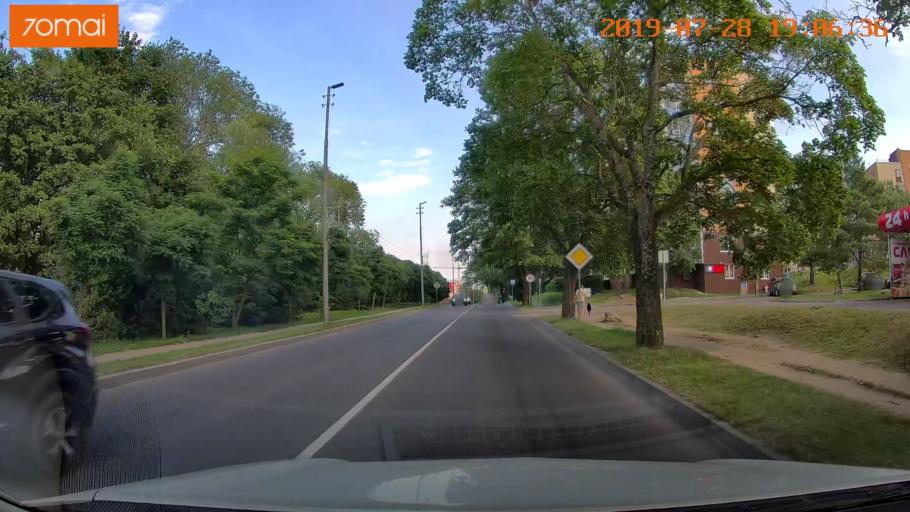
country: RU
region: Kaliningrad
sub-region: Gorod Svetlogorsk
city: Svetlogorsk
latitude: 54.9305
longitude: 20.1662
